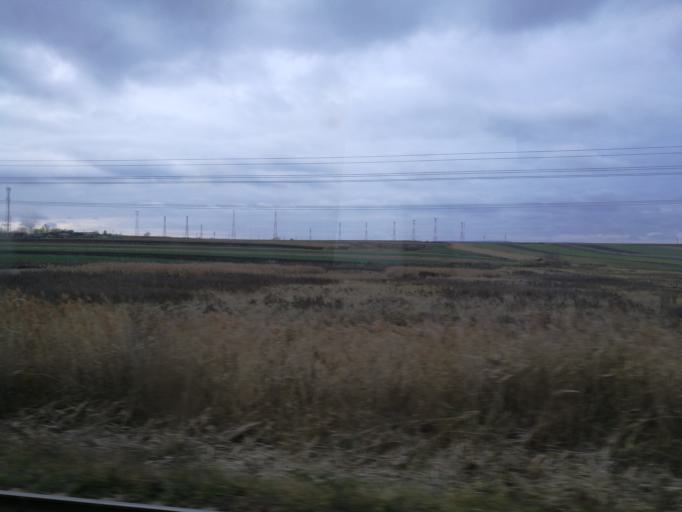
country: RO
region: Bacau
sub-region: Comuna Filipesti
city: Filipesti
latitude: 46.7573
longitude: 26.8809
